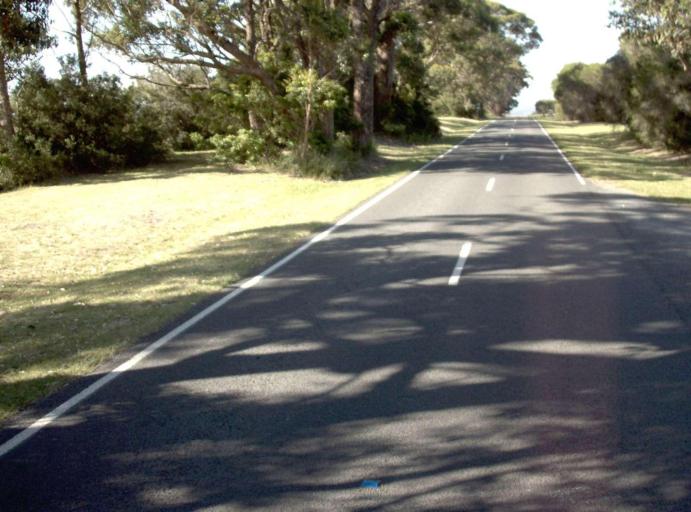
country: AU
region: Victoria
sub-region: East Gippsland
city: Lakes Entrance
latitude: -37.7909
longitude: 148.5353
